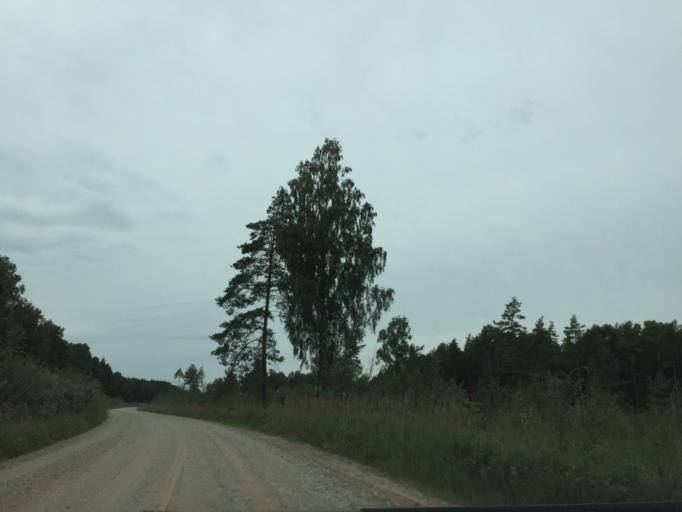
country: LV
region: Jaunpils
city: Jaunpils
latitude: 56.7339
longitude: 23.0970
